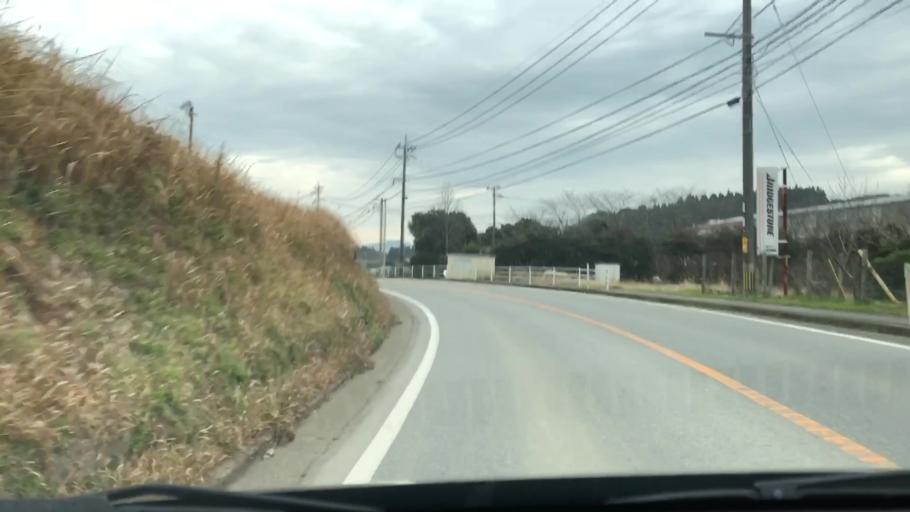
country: JP
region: Oita
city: Usuki
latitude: 33.0190
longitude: 131.6765
